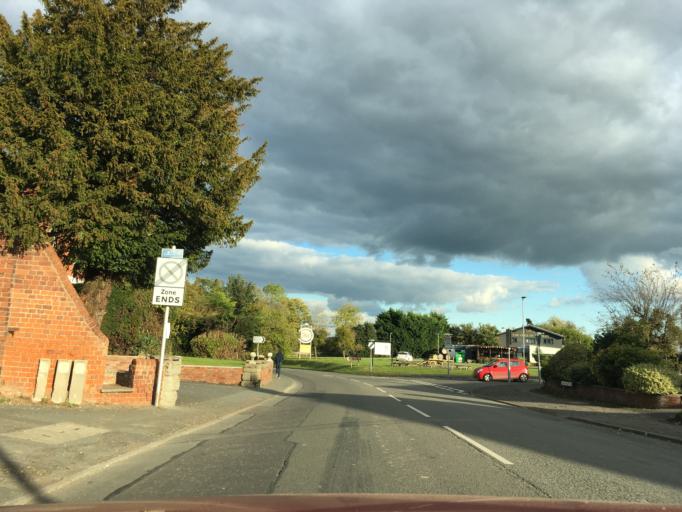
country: GB
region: England
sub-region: Herefordshire
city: Lower Bullingham
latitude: 52.0587
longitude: -2.6818
